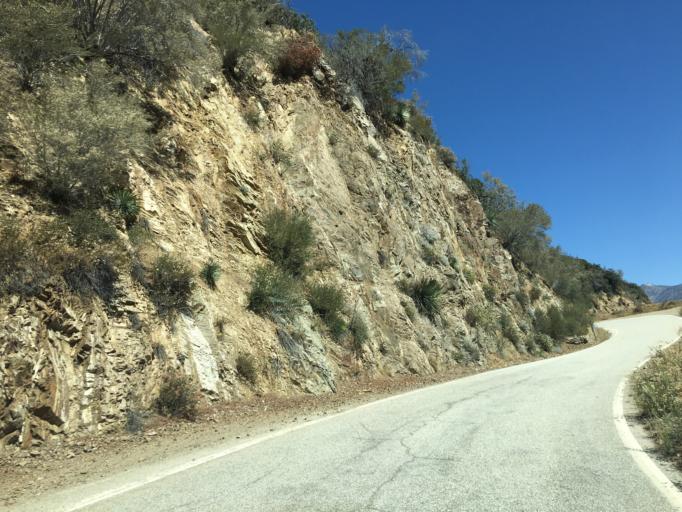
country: US
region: California
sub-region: San Bernardino County
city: San Antonio Heights
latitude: 34.2186
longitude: -117.7538
